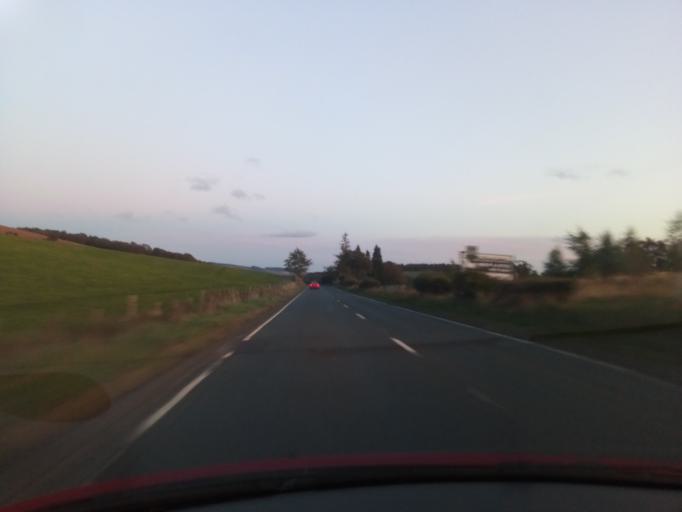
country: GB
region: Scotland
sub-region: The Scottish Borders
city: Lauder
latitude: 55.7783
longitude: -2.8025
